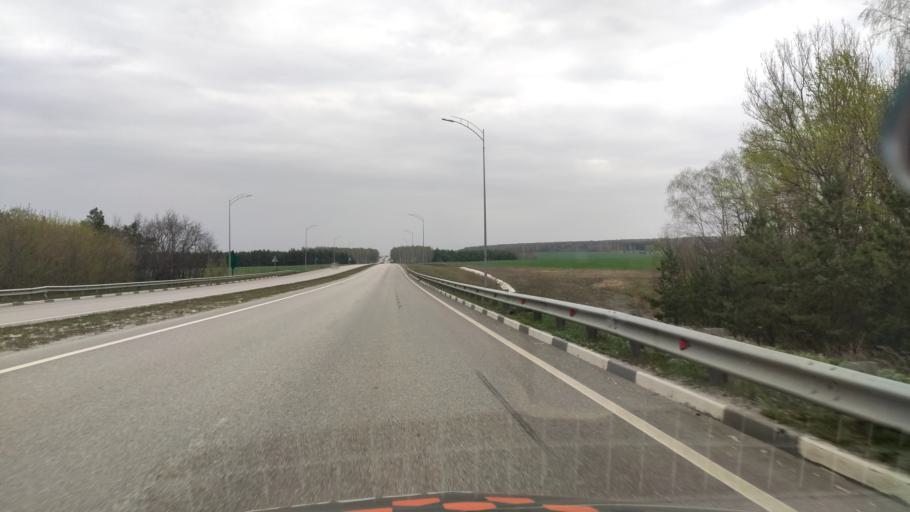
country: RU
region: Belgorod
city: Staryy Oskol
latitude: 51.4020
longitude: 37.8767
